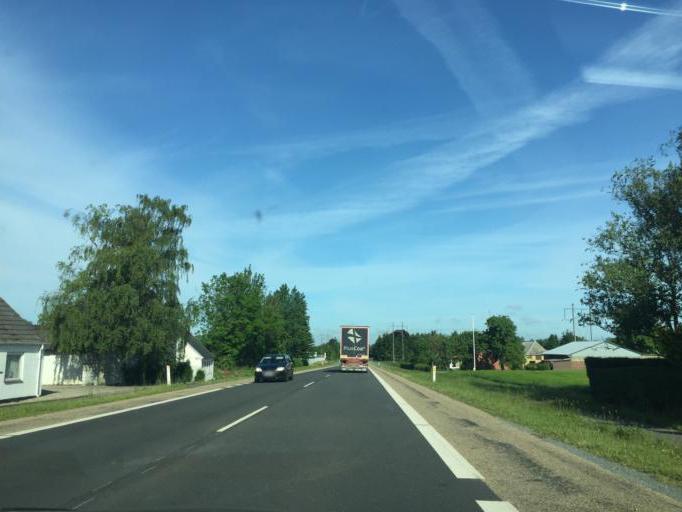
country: DK
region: South Denmark
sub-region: Middelfart Kommune
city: Norre Aby
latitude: 55.4721
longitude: 9.8828
